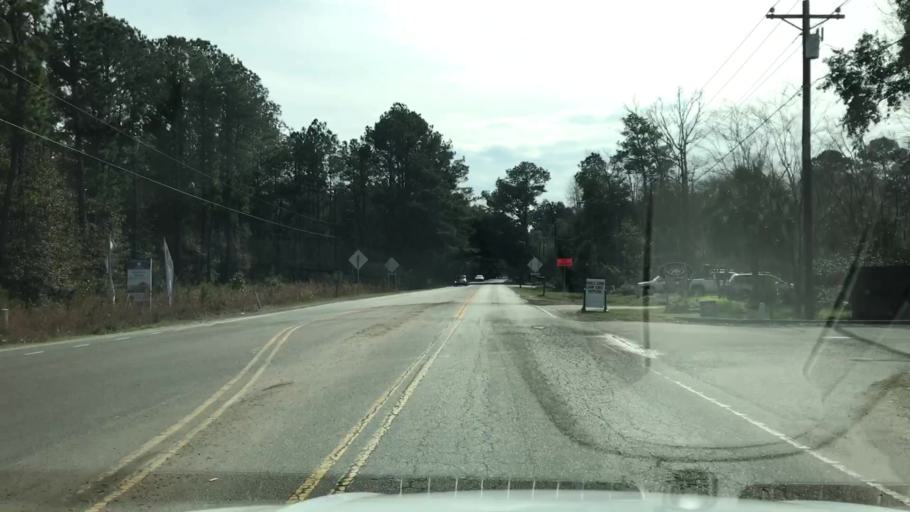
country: US
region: South Carolina
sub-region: Charleston County
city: Shell Point
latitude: 32.7429
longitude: -80.0378
